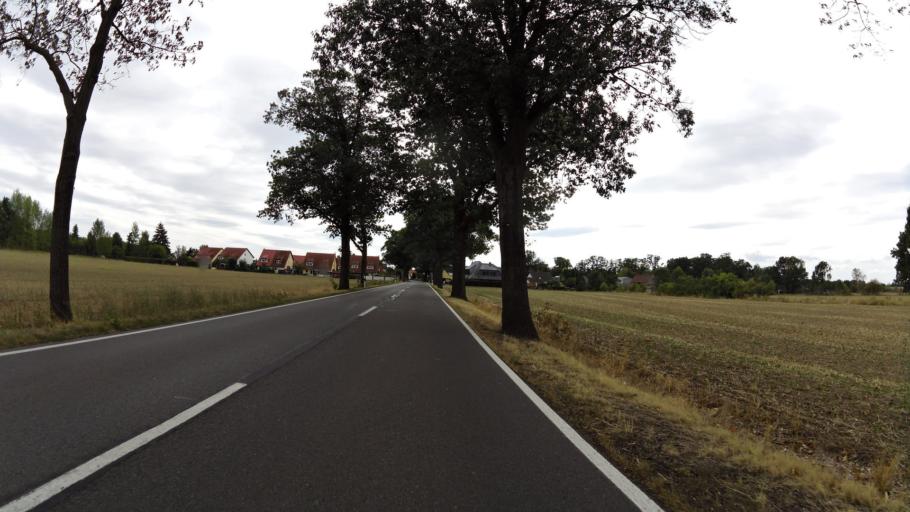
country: DE
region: Brandenburg
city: Cottbus
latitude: 51.7256
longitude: 14.4166
